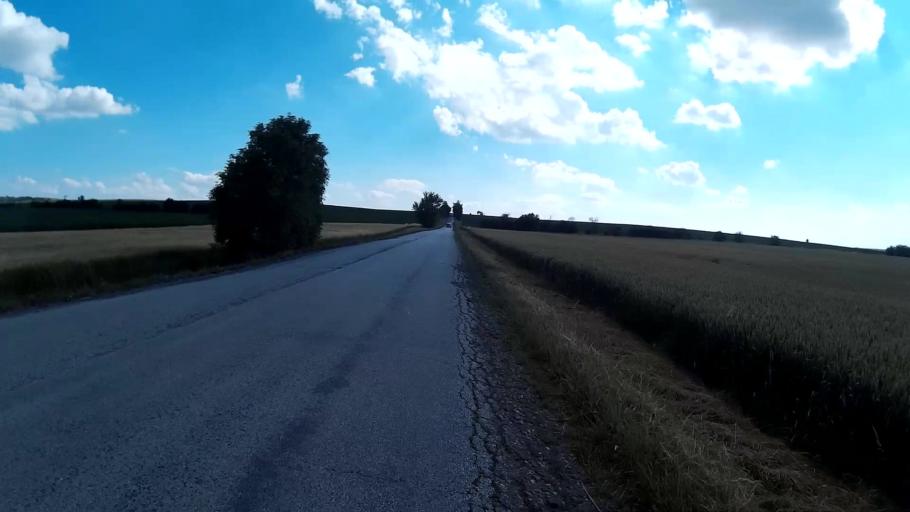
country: CZ
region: South Moravian
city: Krepice
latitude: 49.0241
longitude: 16.7112
